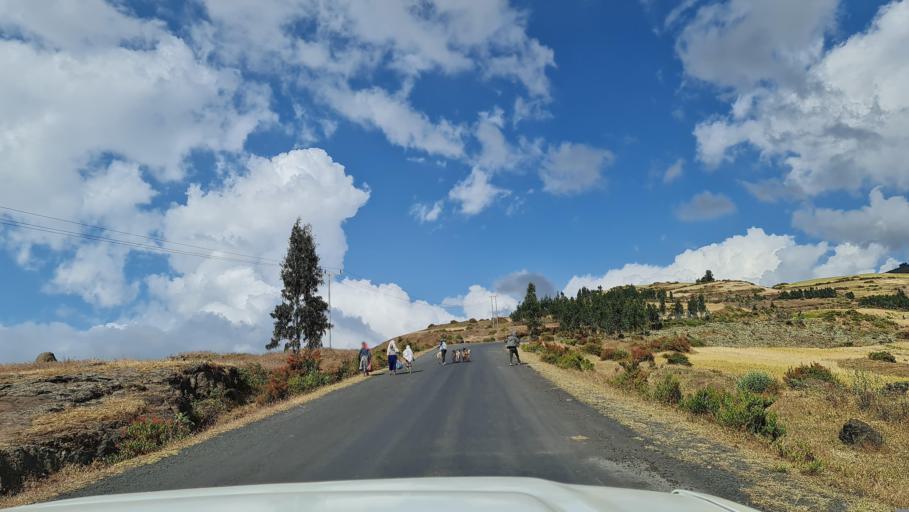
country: ET
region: Amhara
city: Debark'
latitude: 13.1348
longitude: 37.9322
